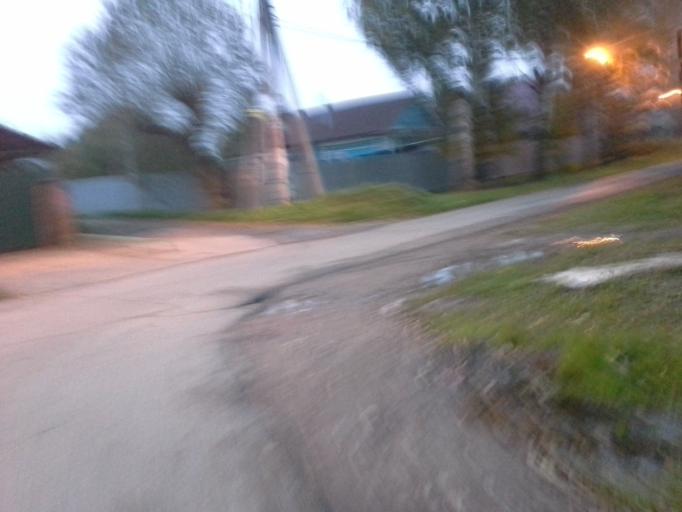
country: RU
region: Moskovskaya
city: Nazar'yevo
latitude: 55.6926
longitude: 37.0334
